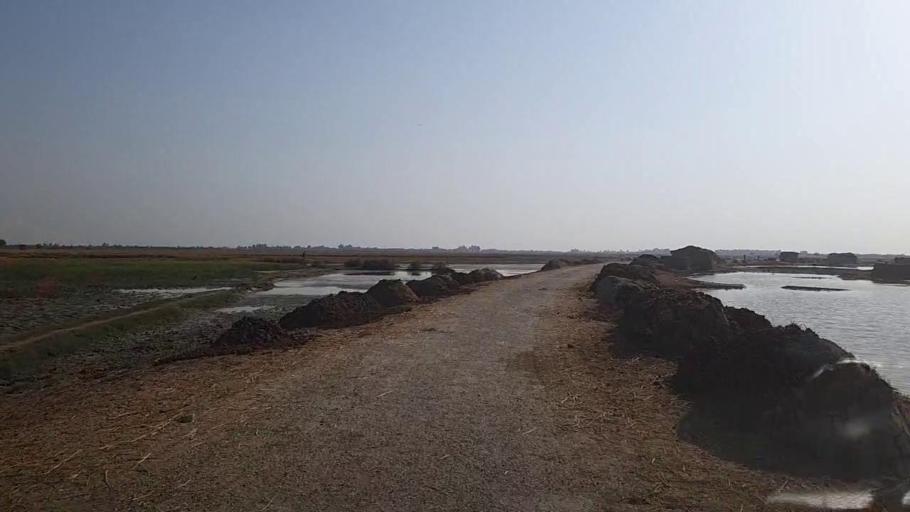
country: PK
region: Sindh
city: Kandhkot
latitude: 28.3695
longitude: 69.3330
